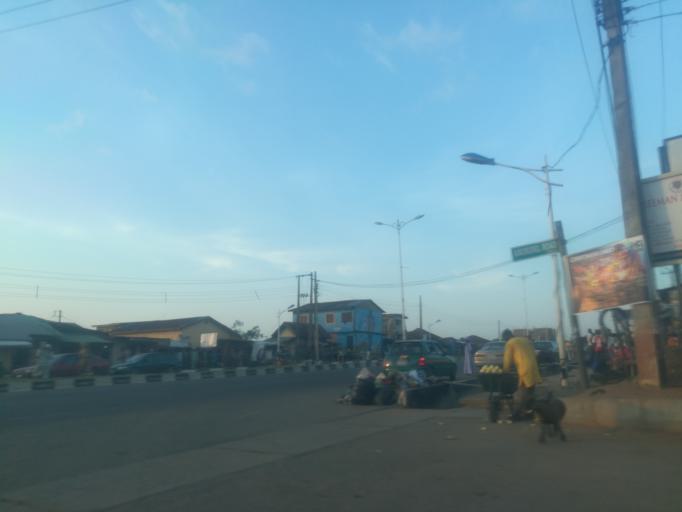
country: NG
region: Ogun
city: Abeokuta
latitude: 7.1496
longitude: 3.3297
